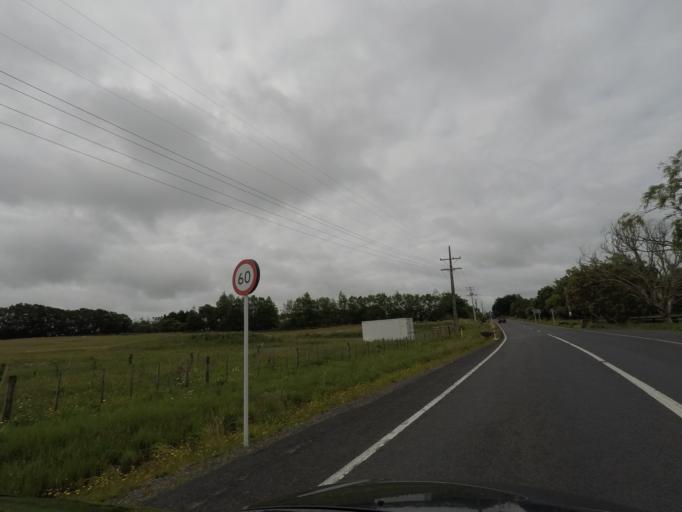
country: NZ
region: Auckland
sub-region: Auckland
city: Rosebank
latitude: -36.7887
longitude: 174.5760
